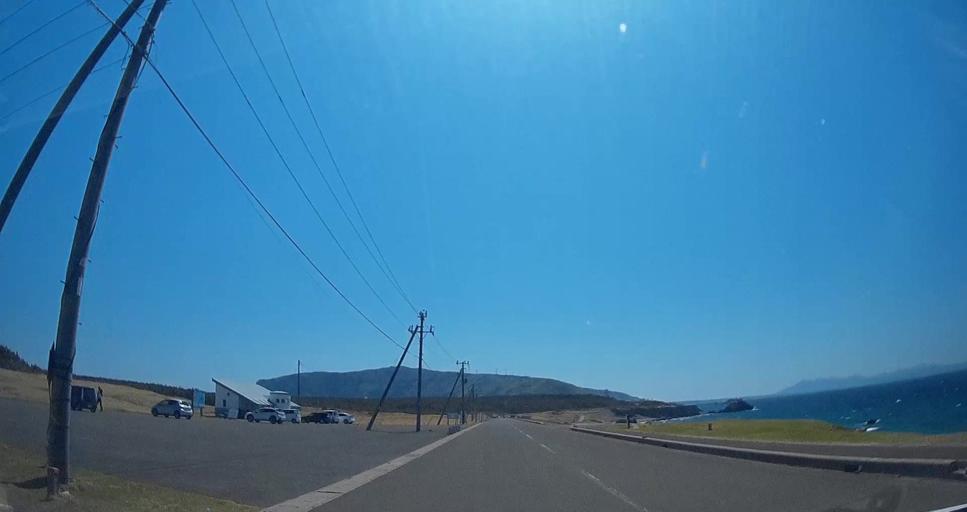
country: JP
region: Aomori
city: Mutsu
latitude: 41.4281
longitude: 141.4600
